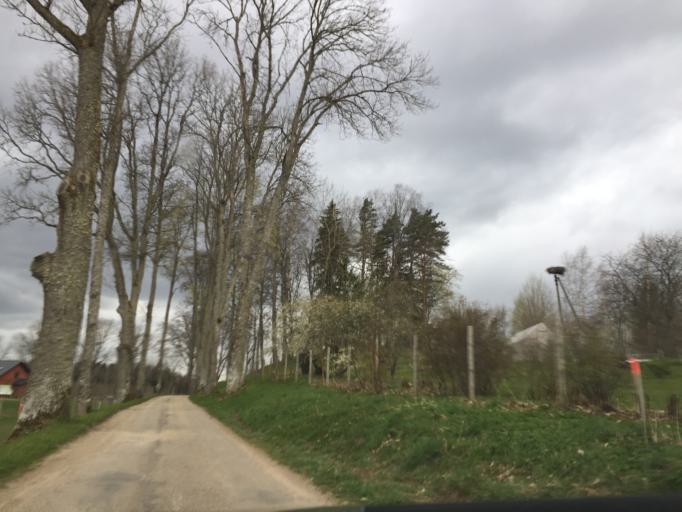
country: LV
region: Aluksnes Rajons
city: Aluksne
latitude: 57.4023
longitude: 27.0368
